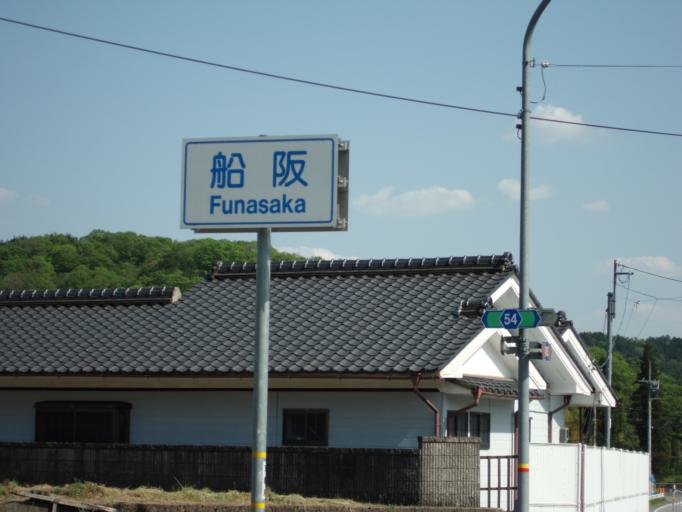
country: JP
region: Kyoto
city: Kameoka
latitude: 35.1078
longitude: 135.4422
